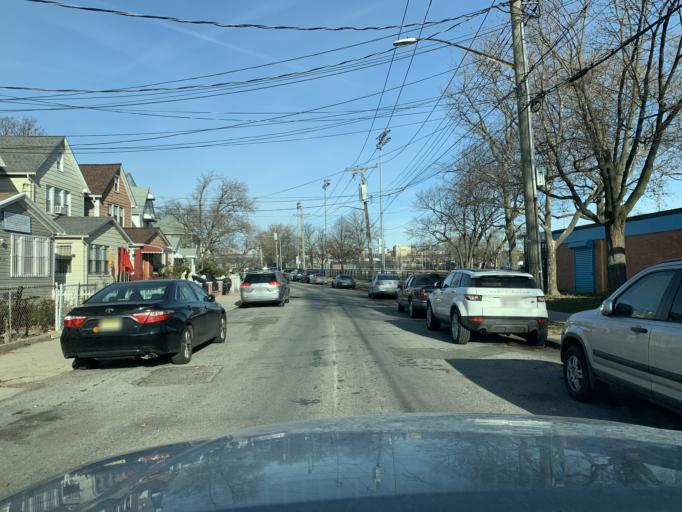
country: US
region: New York
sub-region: Queens County
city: Jamaica
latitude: 40.7016
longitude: -73.7845
